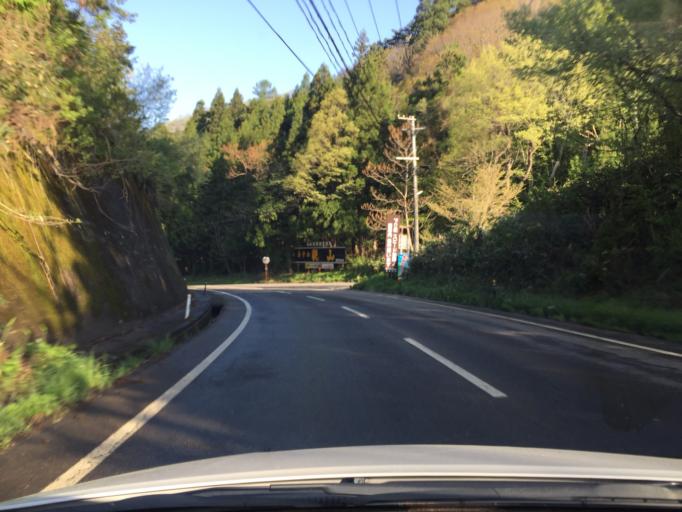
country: JP
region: Fukushima
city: Kitakata
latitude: 37.6687
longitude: 139.9953
